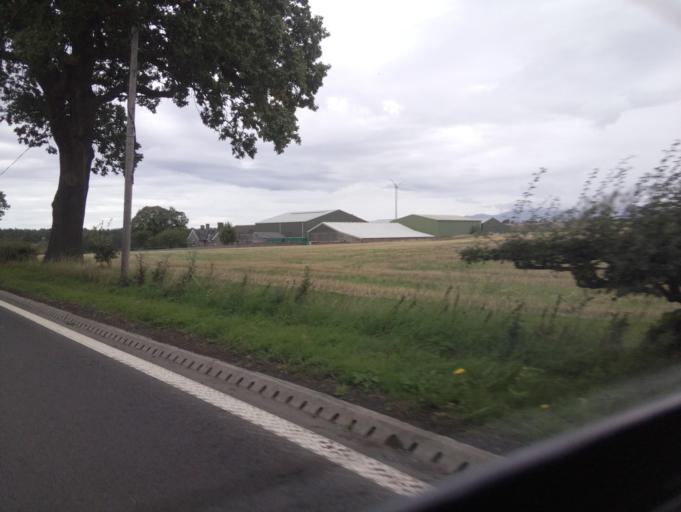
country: GB
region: Scotland
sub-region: Fife
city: High Valleyfield
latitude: 56.0662
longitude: -3.6387
